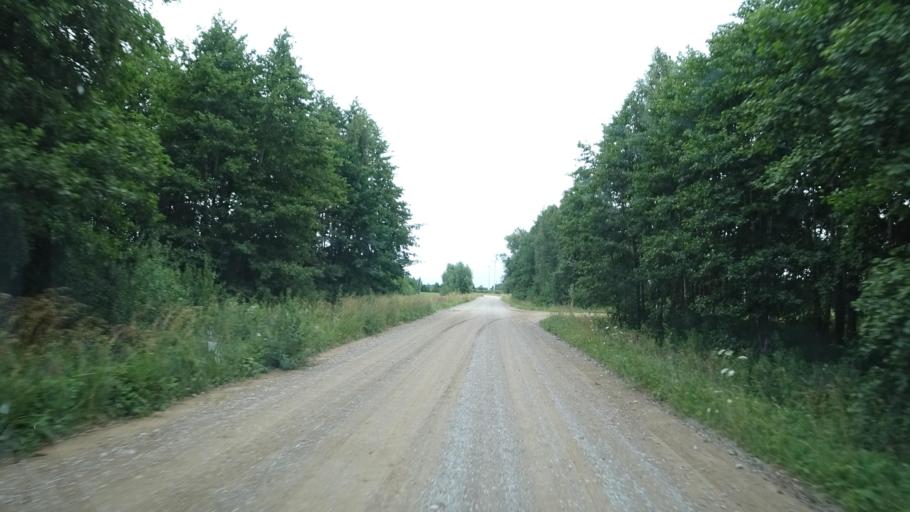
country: LV
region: Liepaja
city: Vec-Liepaja
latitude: 56.6259
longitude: 21.0463
